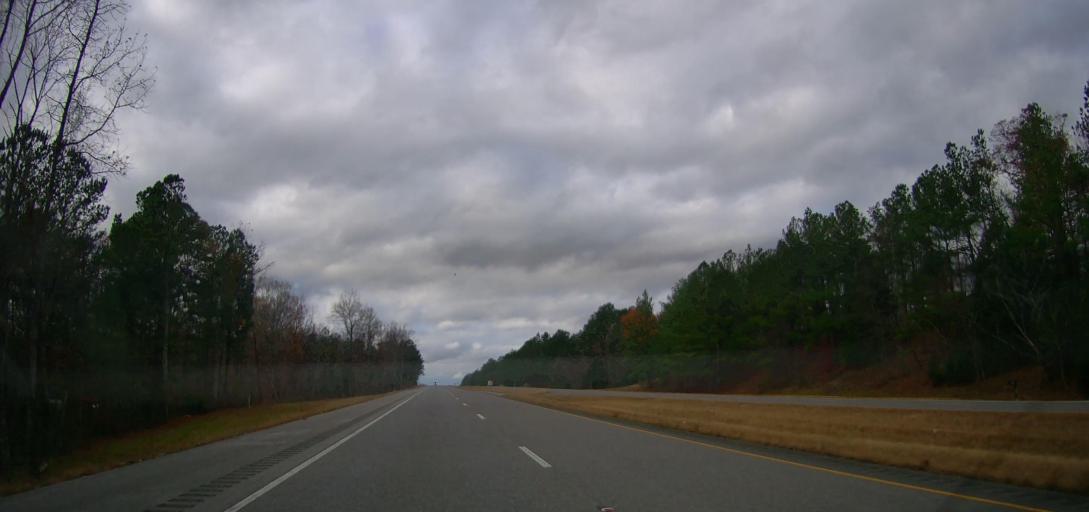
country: US
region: Alabama
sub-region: Lawrence County
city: Town Creek
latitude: 34.6179
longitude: -87.4653
